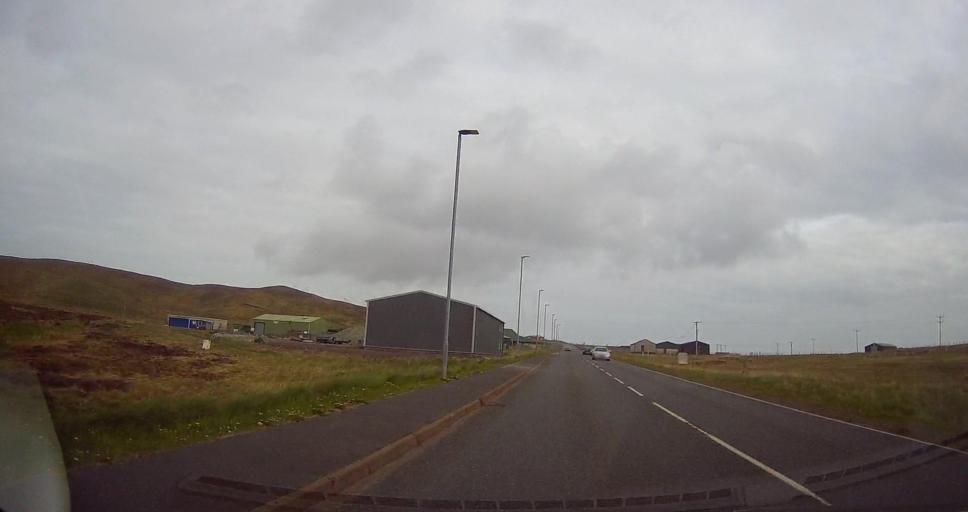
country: GB
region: Scotland
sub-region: Shetland Islands
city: Sandwick
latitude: 60.0563
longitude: -1.2253
